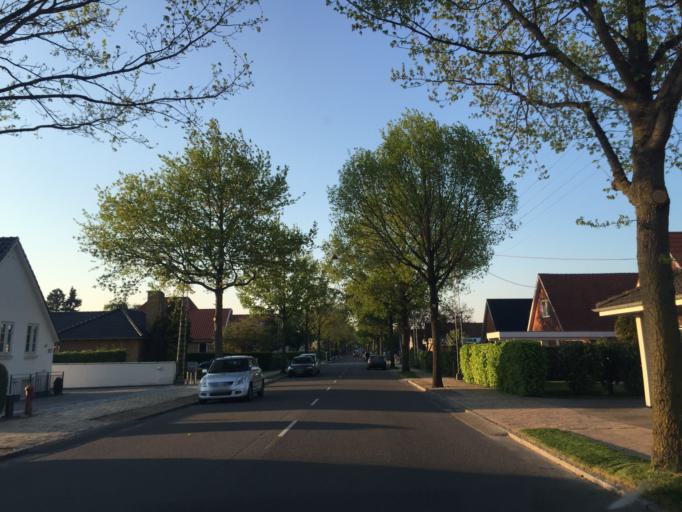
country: DK
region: South Denmark
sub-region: Odense Kommune
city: Odense
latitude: 55.3745
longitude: 10.3878
